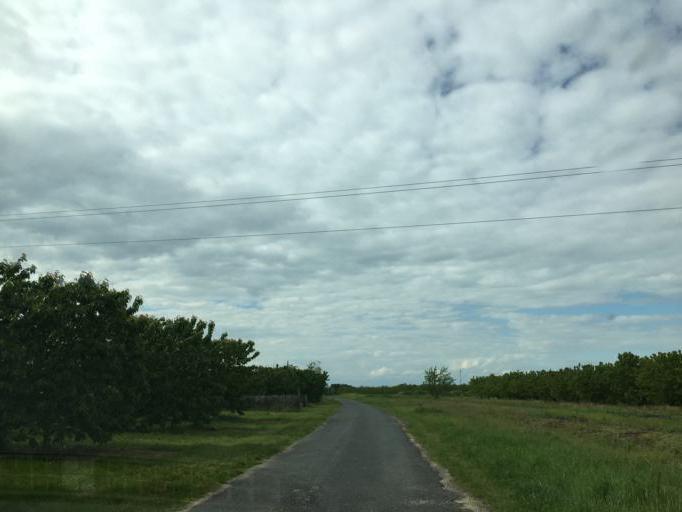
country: FR
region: Centre
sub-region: Departement du Loiret
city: Saint-Hilaire-Saint-Mesmin
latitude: 47.8558
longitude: 1.8460
